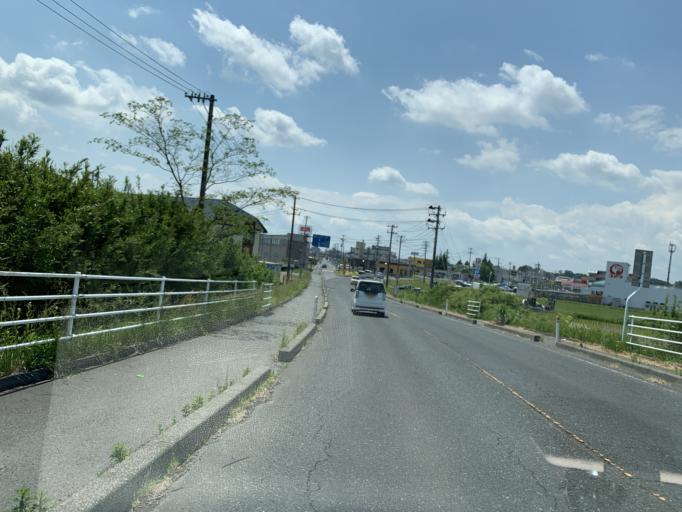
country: JP
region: Miyagi
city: Kogota
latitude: 38.5479
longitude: 141.0610
